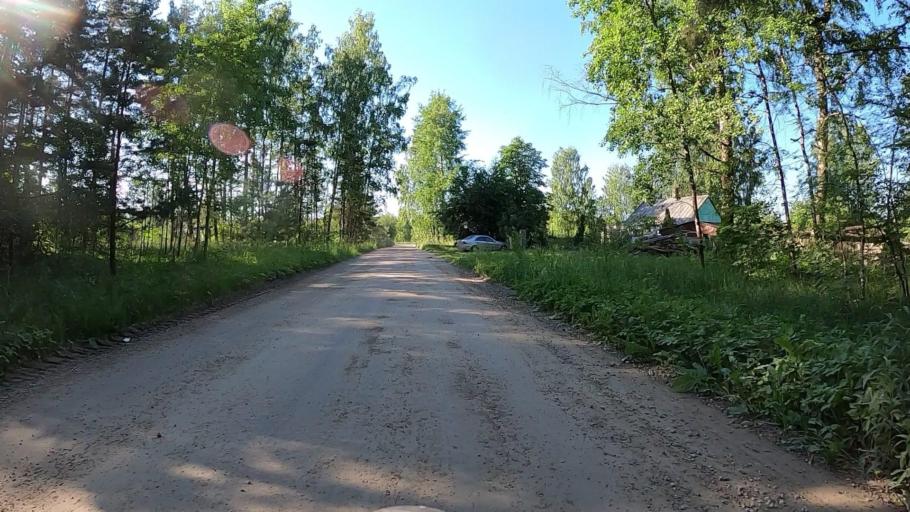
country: LV
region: Kekava
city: Kekava
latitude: 56.8775
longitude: 24.2669
